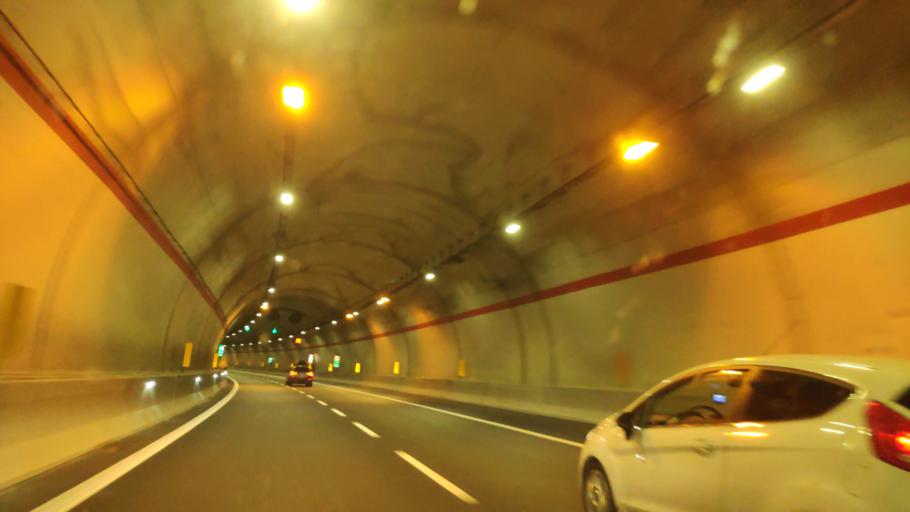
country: IT
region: Calabria
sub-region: Provincia di Cosenza
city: Laino Borgo
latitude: 39.9464
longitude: 15.9588
